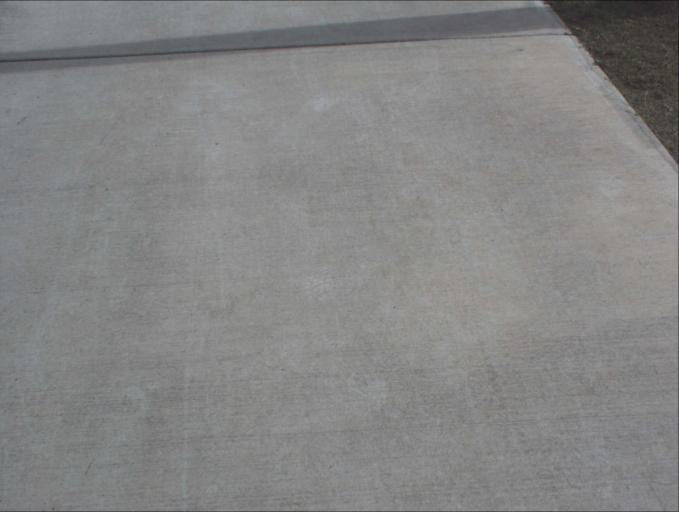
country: AU
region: Queensland
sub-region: Logan
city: Chambers Flat
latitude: -27.8028
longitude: 153.1088
